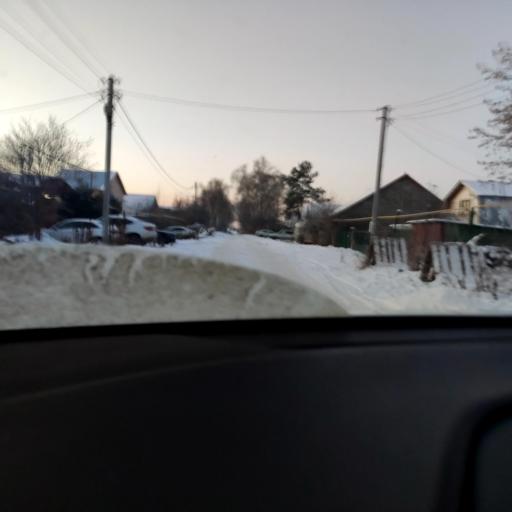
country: RU
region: Tatarstan
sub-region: Gorod Kazan'
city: Kazan
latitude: 55.7429
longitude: 49.0993
